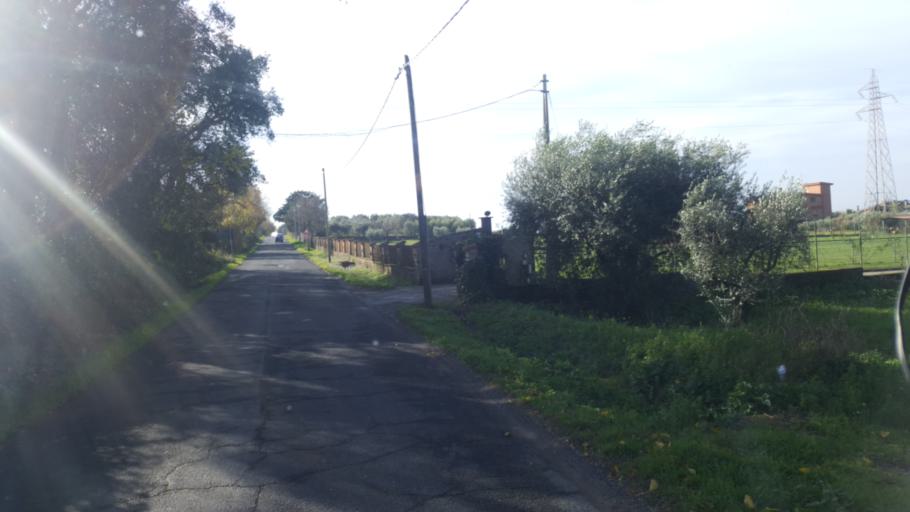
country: IT
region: Latium
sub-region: Citta metropolitana di Roma Capitale
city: Mantiglia di Ardea
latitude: 41.6697
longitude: 12.6364
